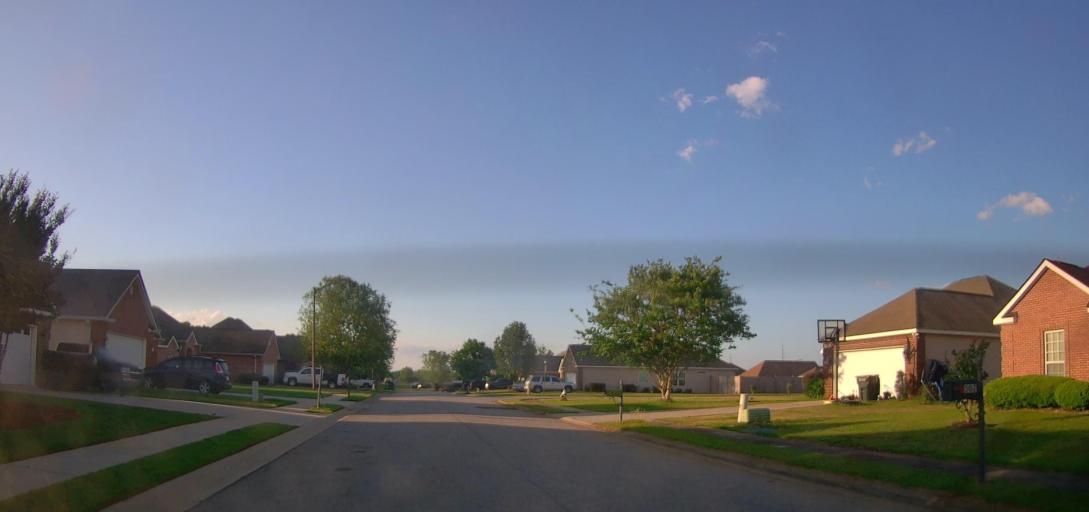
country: US
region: Georgia
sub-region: Houston County
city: Centerville
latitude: 32.6275
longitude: -83.7115
